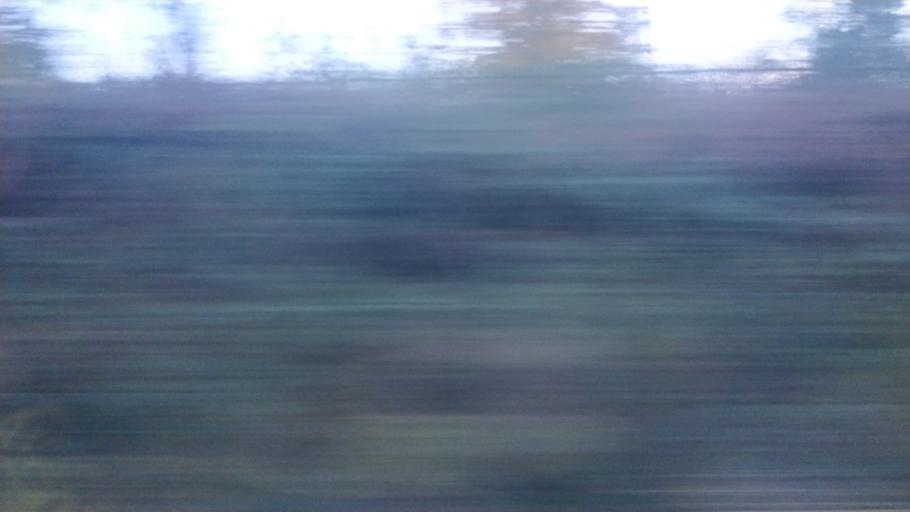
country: GB
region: England
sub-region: Lancashire
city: Appley Bridge
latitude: 53.5838
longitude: -2.7404
